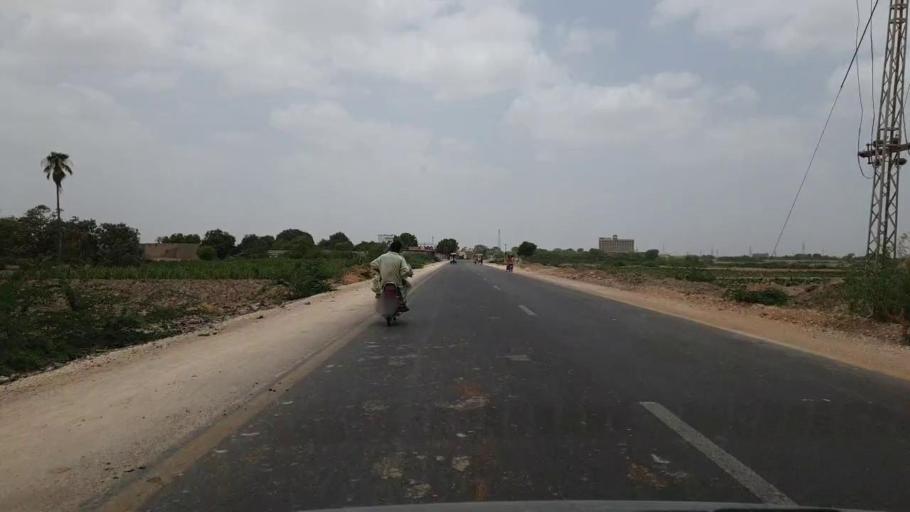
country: PK
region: Sindh
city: Naukot
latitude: 24.8436
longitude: 69.4271
